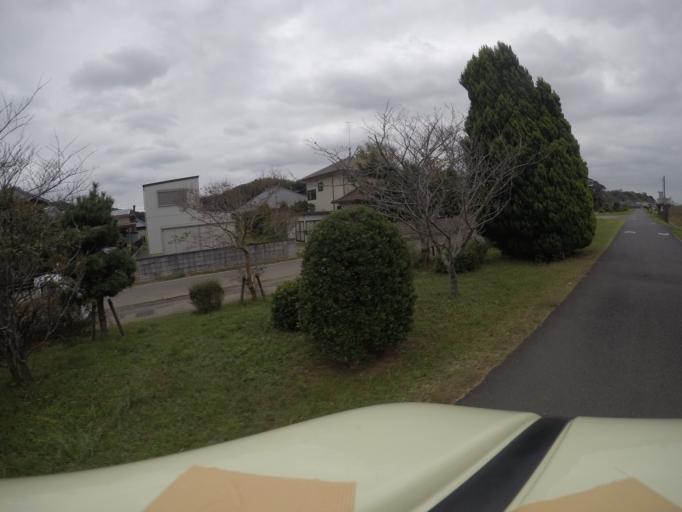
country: JP
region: Ibaraki
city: Itako
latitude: 35.9777
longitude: 140.4979
